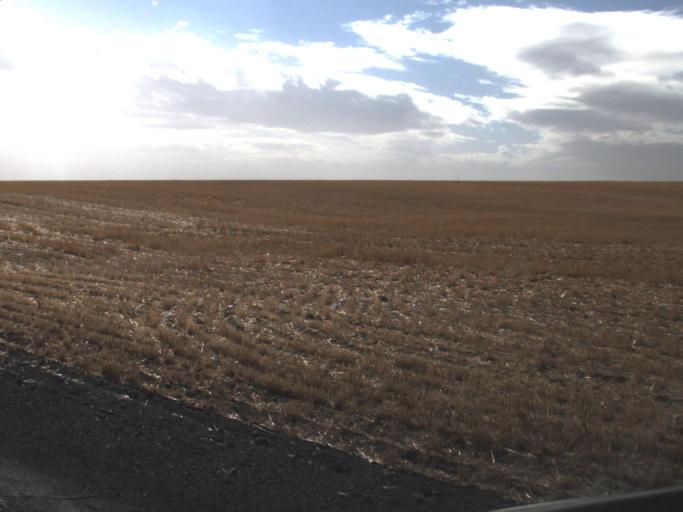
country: US
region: Washington
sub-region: Okanogan County
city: Coulee Dam
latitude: 47.5738
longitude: -118.7859
